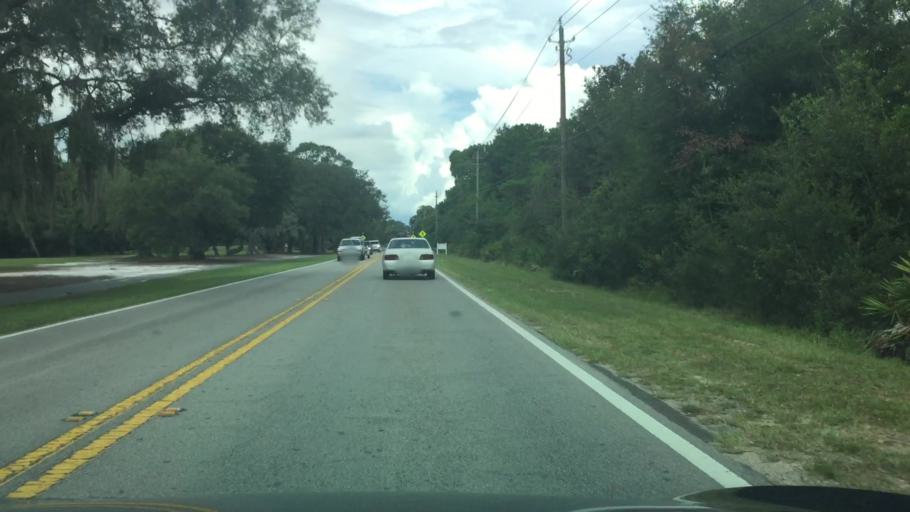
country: US
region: Florida
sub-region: Bay County
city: Upper Grand Lagoon
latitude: 30.1555
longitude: -85.7300
